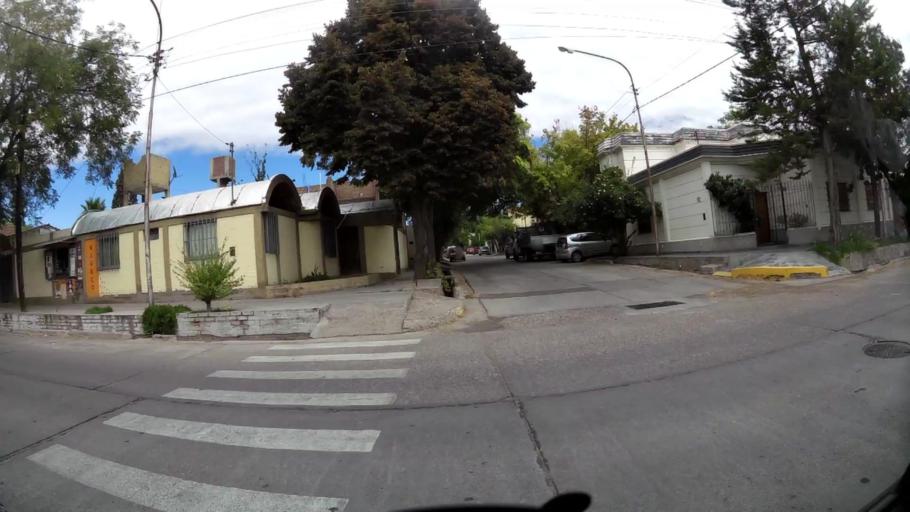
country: AR
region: Mendoza
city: Las Heras
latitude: -32.8627
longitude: -68.8551
